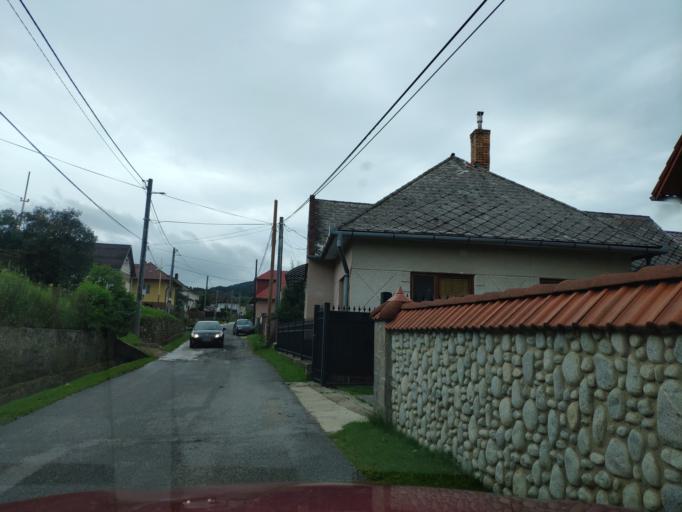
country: SK
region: Presovsky
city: Sabinov
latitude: 49.0455
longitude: 21.0170
